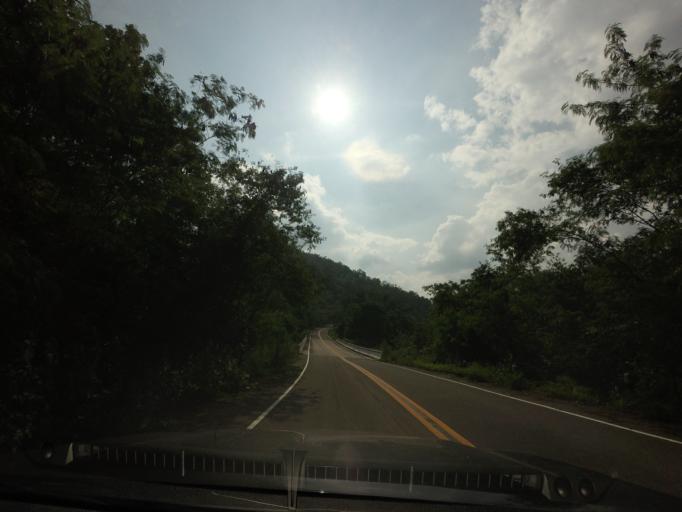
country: TH
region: Nan
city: Na Noi
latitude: 18.2766
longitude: 100.9635
